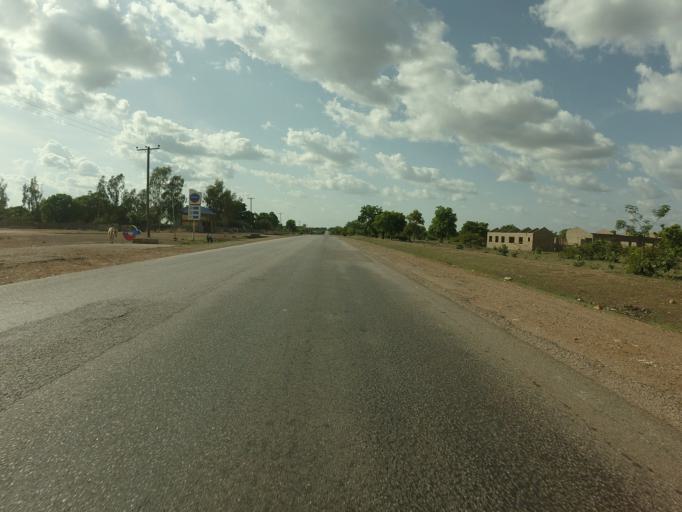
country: GH
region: Upper East
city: Bolgatanga
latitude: 10.6495
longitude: -0.8577
